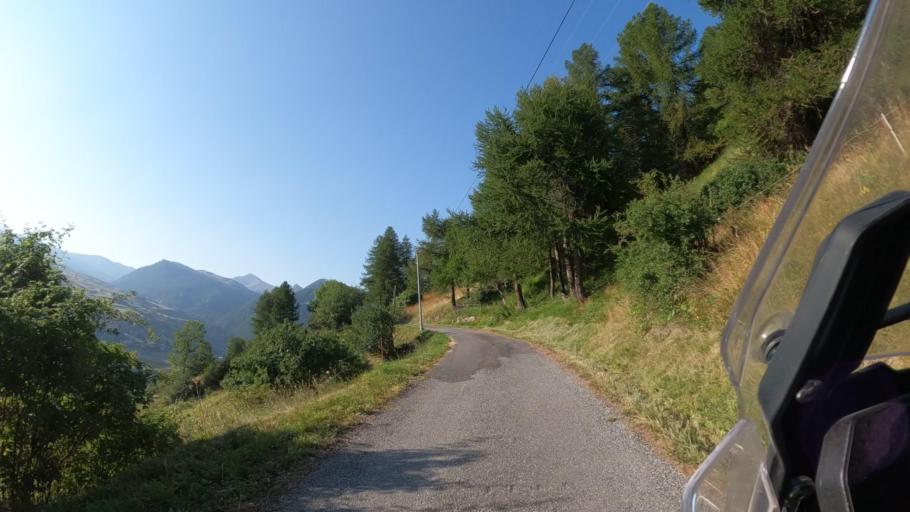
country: FR
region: Provence-Alpes-Cote d'Azur
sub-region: Departement des Hautes-Alpes
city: Guillestre
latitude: 44.6051
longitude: 6.6812
